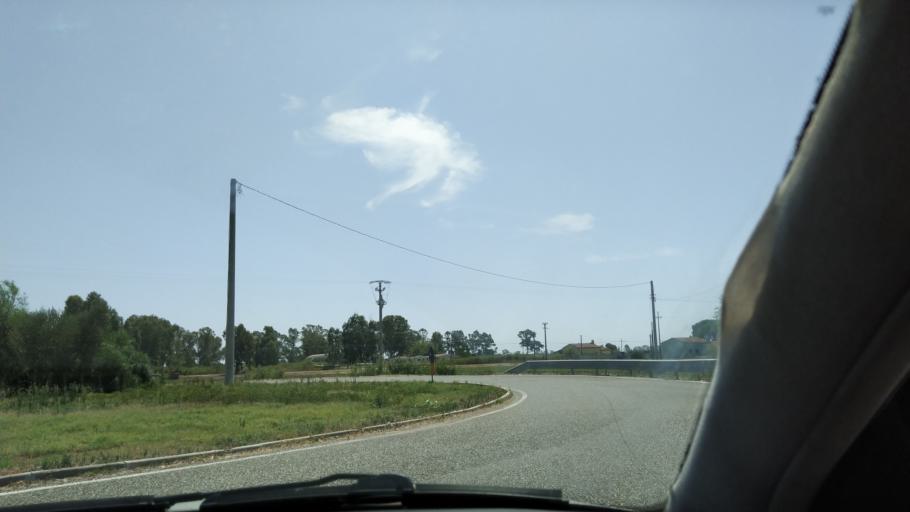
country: IT
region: Basilicate
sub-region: Provincia di Matera
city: Marconia
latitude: 40.3402
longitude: 16.7631
